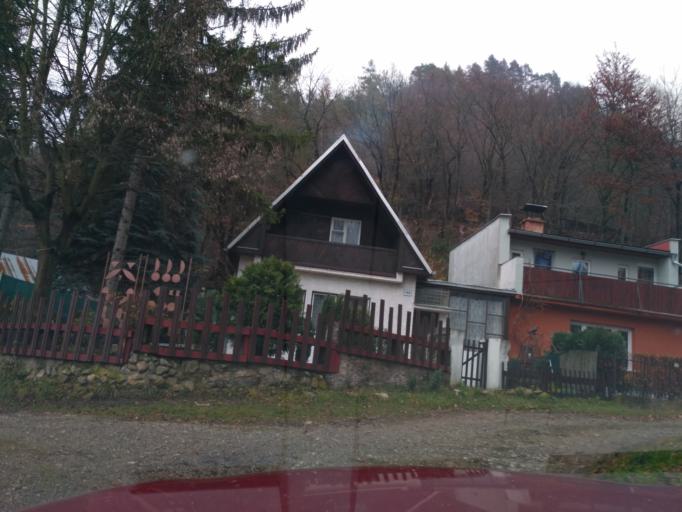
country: SK
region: Kosicky
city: Kosice
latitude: 48.8474
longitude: 21.2319
